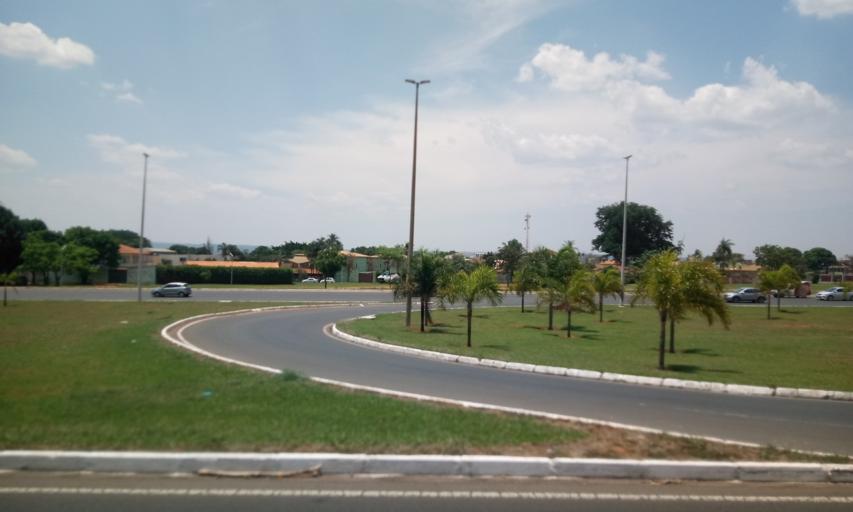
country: BR
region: Federal District
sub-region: Brasilia
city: Brasilia
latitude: -15.7946
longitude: -47.8569
